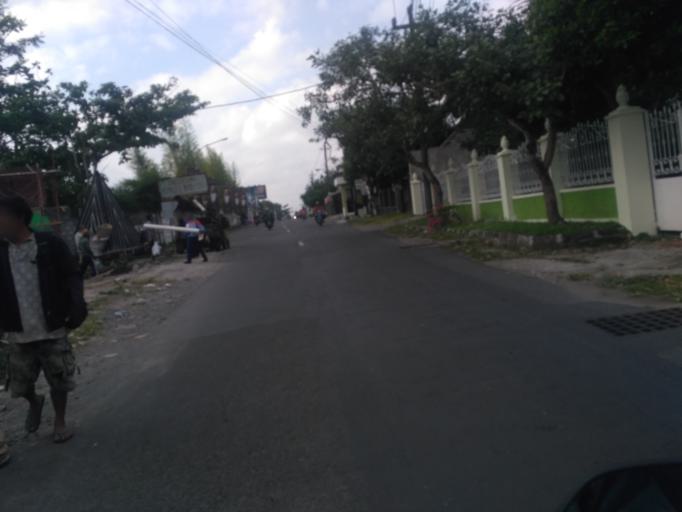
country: ID
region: Daerah Istimewa Yogyakarta
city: Yogyakarta
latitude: -7.7670
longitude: 110.3533
